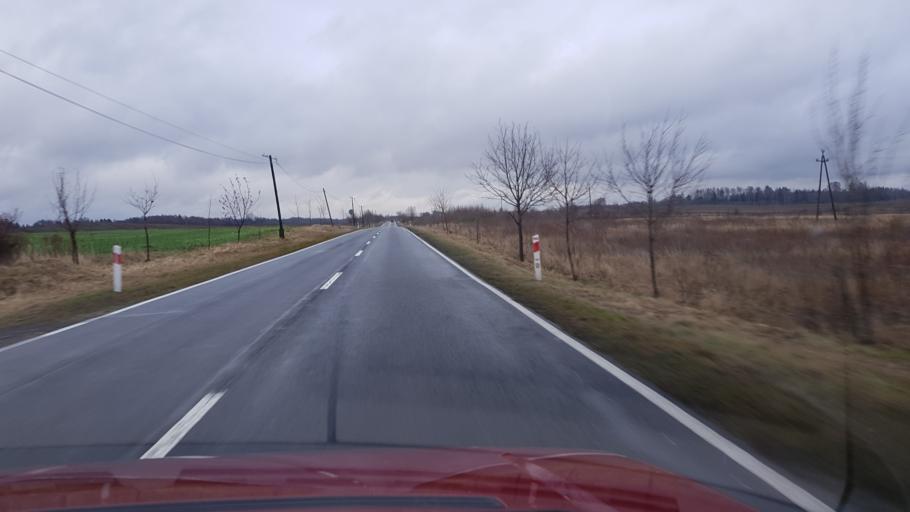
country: PL
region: West Pomeranian Voivodeship
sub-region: Powiat lobeski
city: Wegorzyno
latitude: 53.5319
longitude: 15.5702
